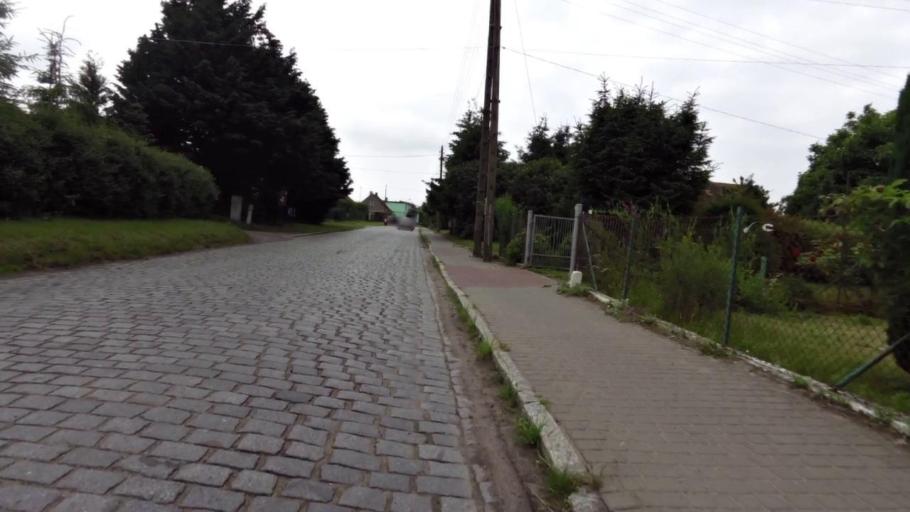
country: PL
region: West Pomeranian Voivodeship
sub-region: Powiat kamienski
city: Wolin
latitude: 53.8433
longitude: 14.6281
